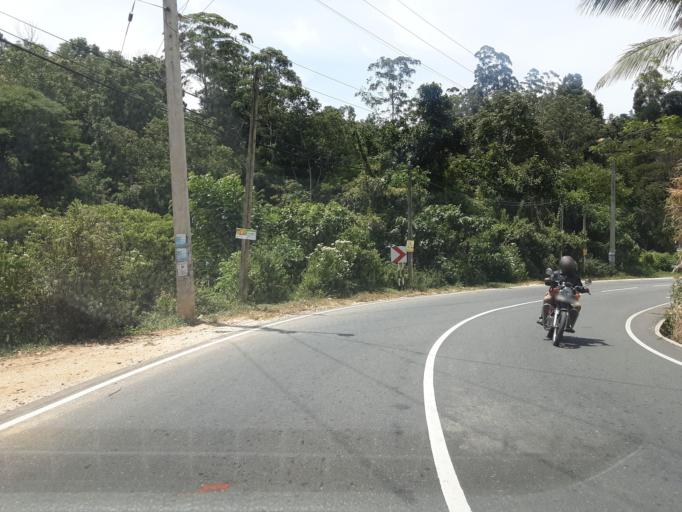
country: LK
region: Uva
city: Badulla
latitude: 6.9623
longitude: 80.9350
